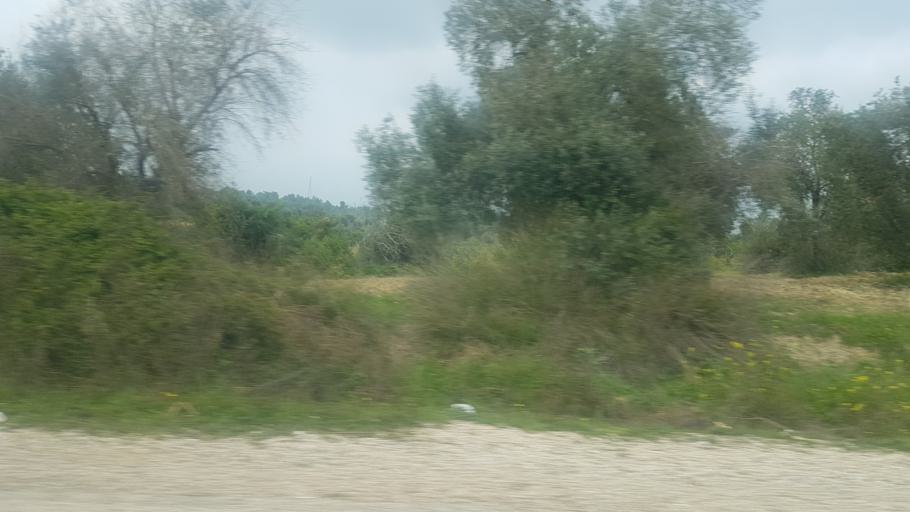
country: TR
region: Adana
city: Seyhan
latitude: 37.0534
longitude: 35.2141
